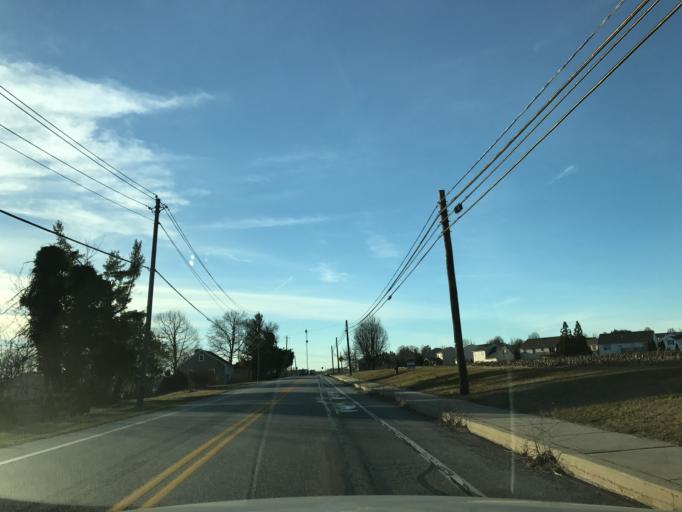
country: US
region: Pennsylvania
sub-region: Lancaster County
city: Maytown
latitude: 40.0637
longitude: -76.5714
